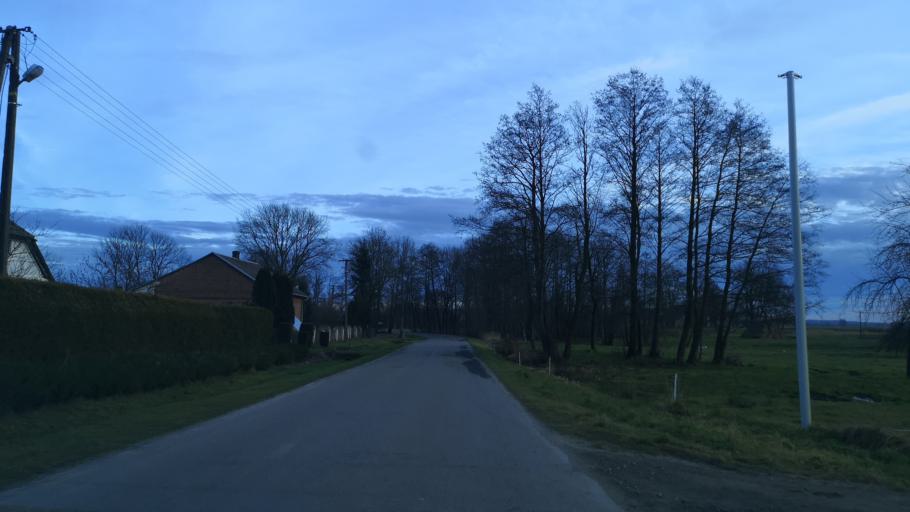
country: PL
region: Subcarpathian Voivodeship
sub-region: Powiat lezajski
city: Piskorowice
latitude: 50.2578
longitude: 22.5984
